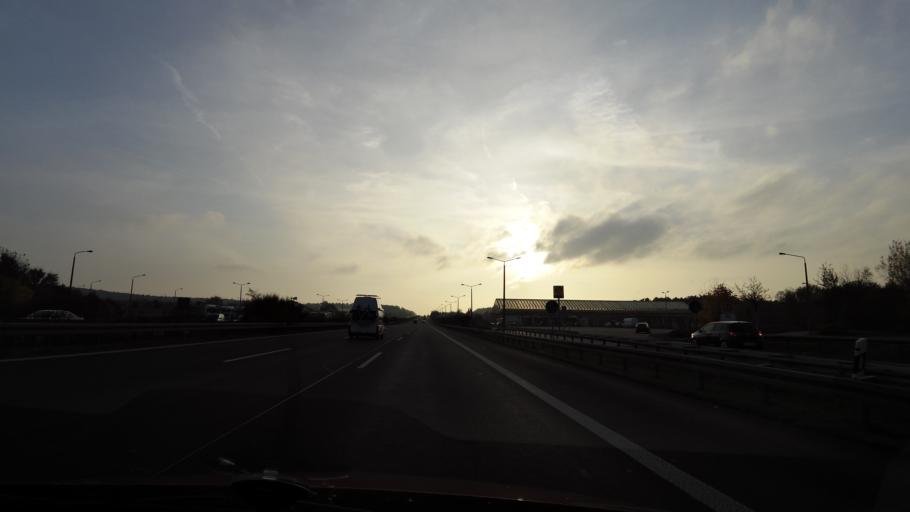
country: DE
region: Brandenburg
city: Linthe
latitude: 52.1352
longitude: 12.7550
